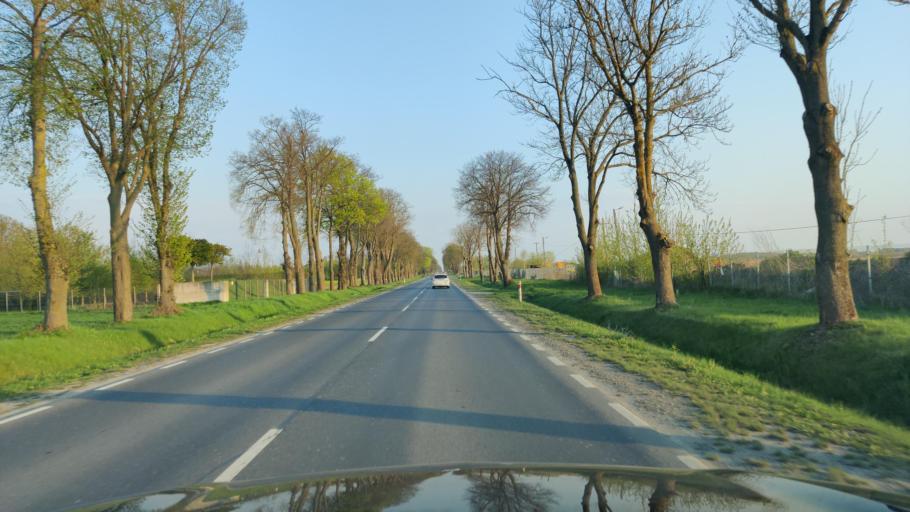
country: PL
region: Masovian Voivodeship
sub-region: Powiat pultuski
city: Pultusk
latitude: 52.6339
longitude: 21.0960
